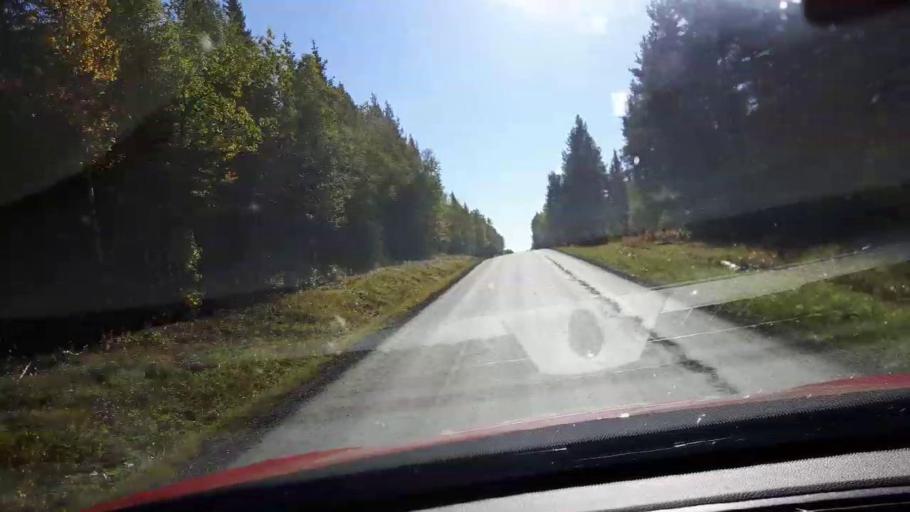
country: NO
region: Nord-Trondelag
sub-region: Lierne
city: Sandvika
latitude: 64.6058
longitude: 13.9630
